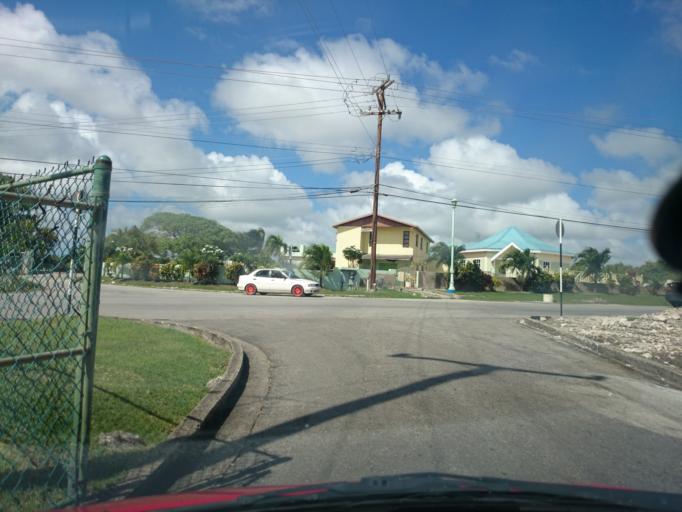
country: BB
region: Saint Philip
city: Crane
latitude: 13.0822
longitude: -59.4869
